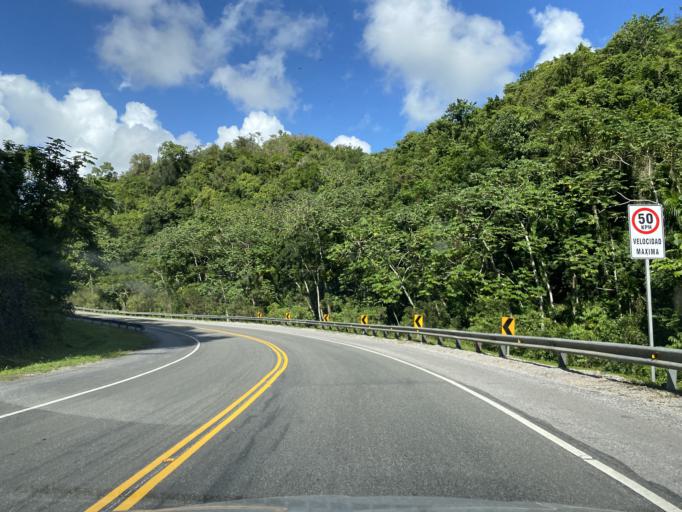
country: DO
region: Monte Plata
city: Majagual
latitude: 19.0768
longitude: -69.8274
